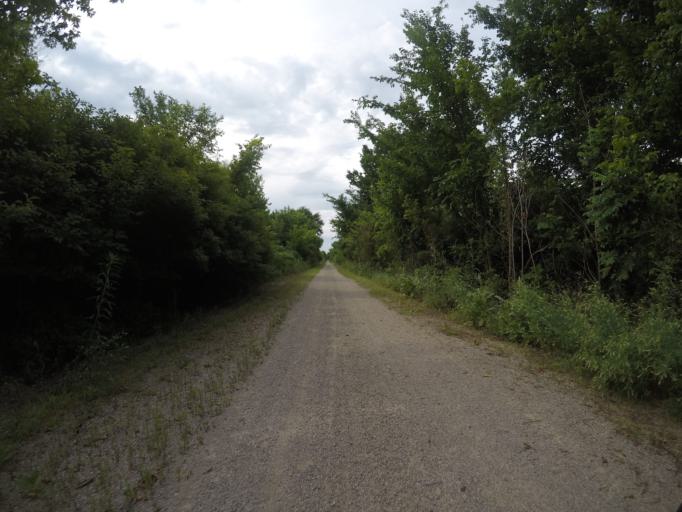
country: US
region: Kansas
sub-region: Anderson County
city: Garnett
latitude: 38.4388
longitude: -95.2641
